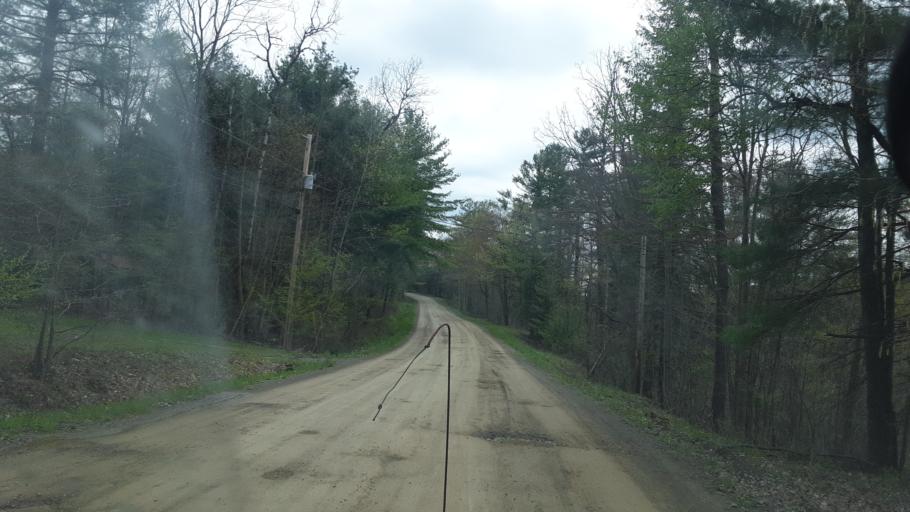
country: US
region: New York
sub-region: Steuben County
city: Addison
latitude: 42.0957
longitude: -77.3289
